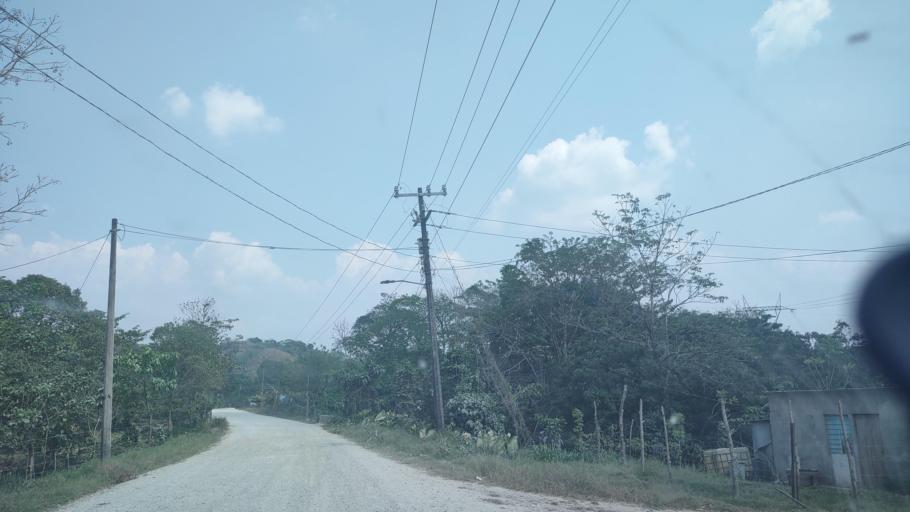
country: MX
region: Tabasco
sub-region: Huimanguillo
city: Francisco Rueda
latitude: 17.5931
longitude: -93.8971
